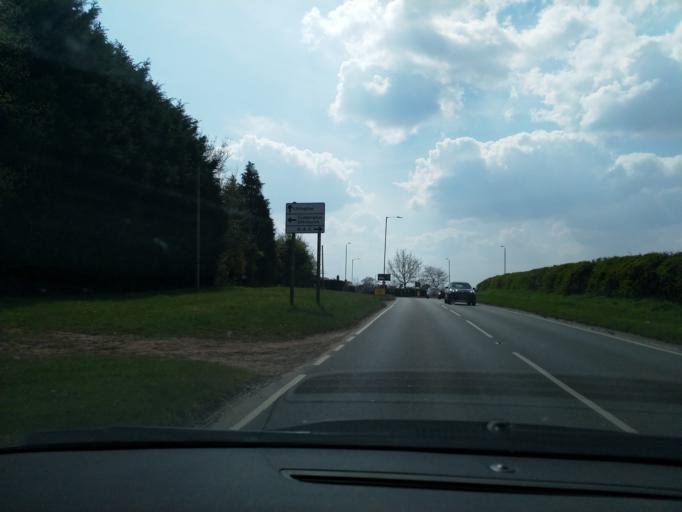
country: GB
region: England
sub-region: Warwickshire
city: Royal Leamington Spa
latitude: 52.3174
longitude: -1.5172
